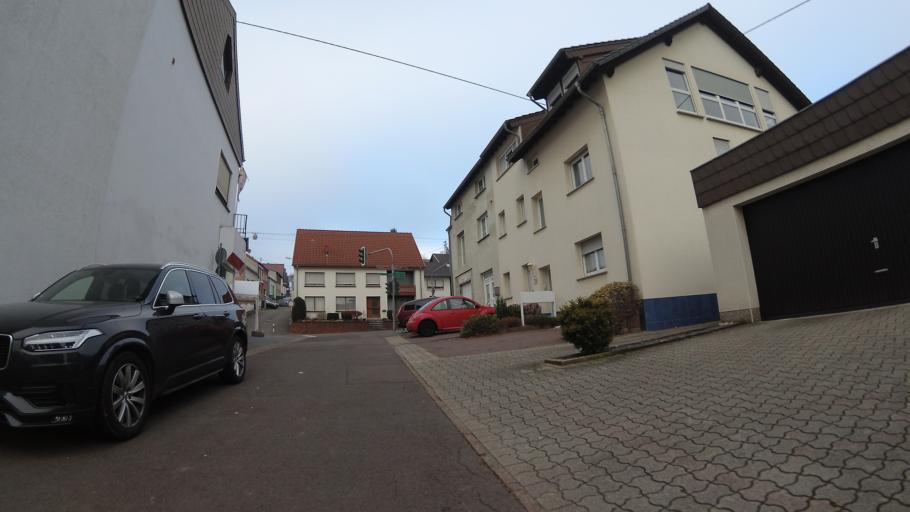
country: DE
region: Saarland
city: Schwalbach
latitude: 49.2970
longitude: 6.8045
